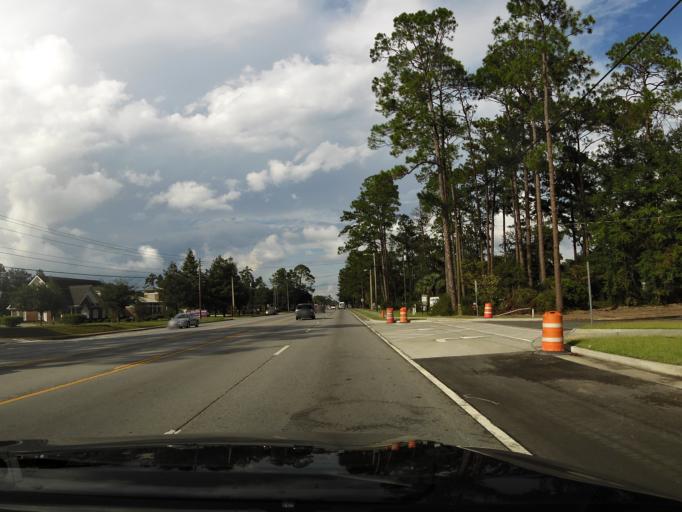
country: US
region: Georgia
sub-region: Liberty County
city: Hinesville
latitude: 31.8304
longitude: -81.5973
